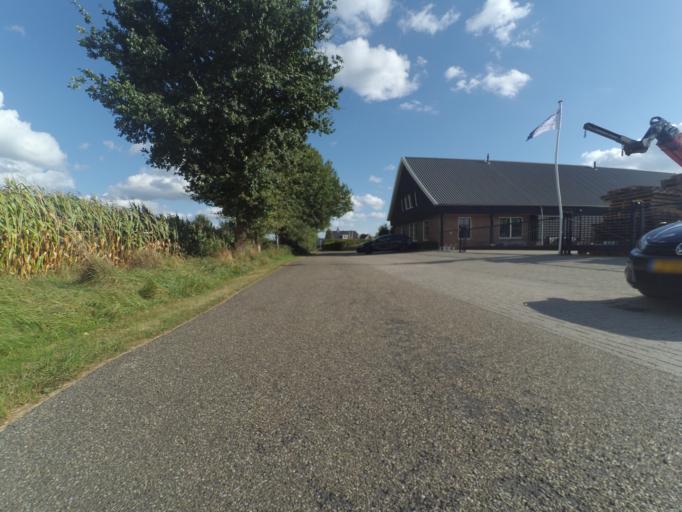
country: NL
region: Gelderland
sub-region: Gemeente Ede
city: Ederveen
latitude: 52.0729
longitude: 5.5726
